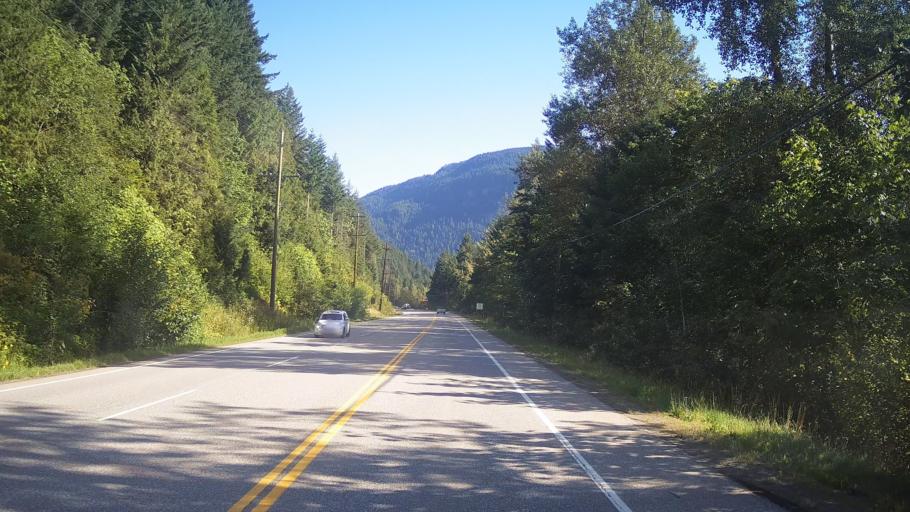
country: CA
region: British Columbia
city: Hope
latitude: 49.6825
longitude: -121.4166
